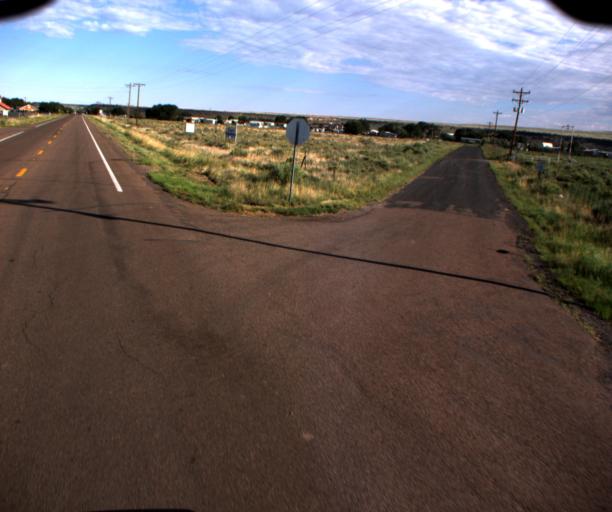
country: US
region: Arizona
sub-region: Apache County
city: Springerville
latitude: 34.1223
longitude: -109.2610
